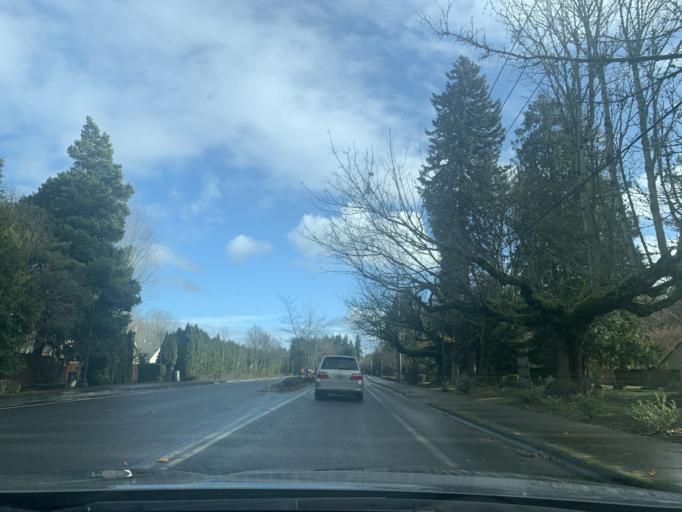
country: US
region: Oregon
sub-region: Washington County
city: Sherwood
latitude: 45.3714
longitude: -122.8524
